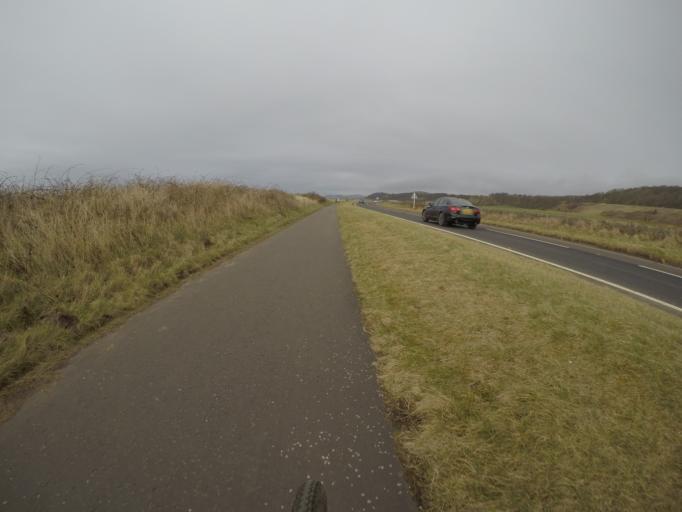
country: GB
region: Scotland
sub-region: North Ayrshire
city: Ardrossan
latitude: 55.6568
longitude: -4.8282
